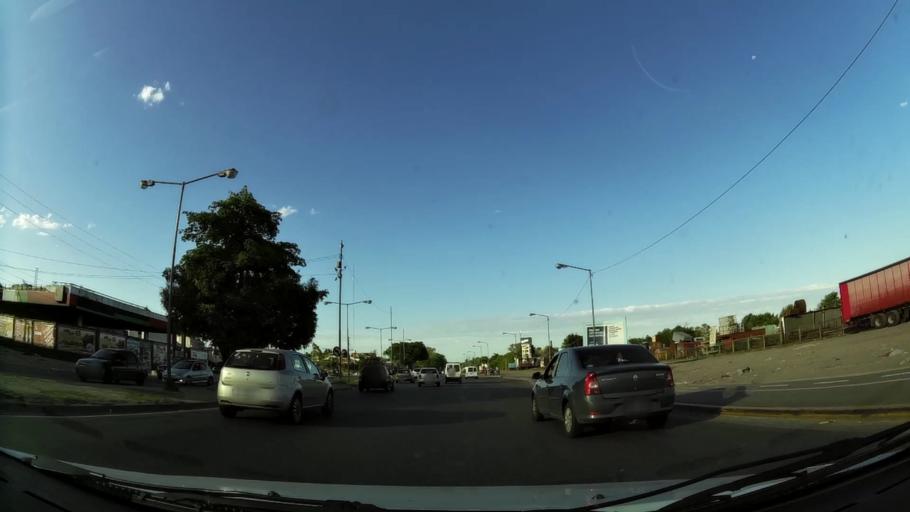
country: AR
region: Buenos Aires
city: Caseros
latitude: -34.5546
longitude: -58.5852
